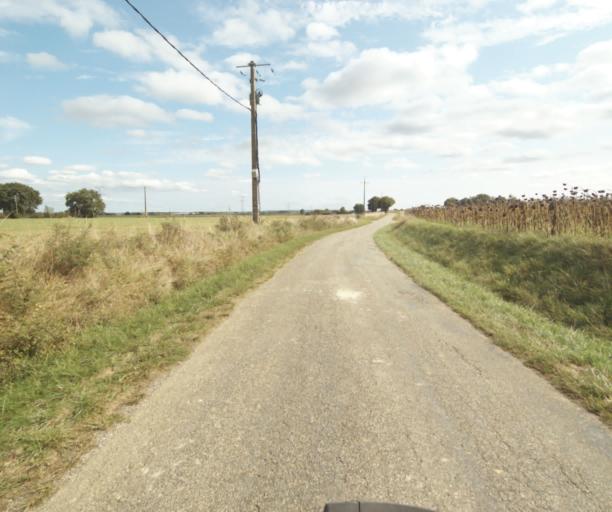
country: FR
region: Midi-Pyrenees
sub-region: Departement du Tarn-et-Garonne
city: Finhan
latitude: 43.8718
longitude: 1.1636
